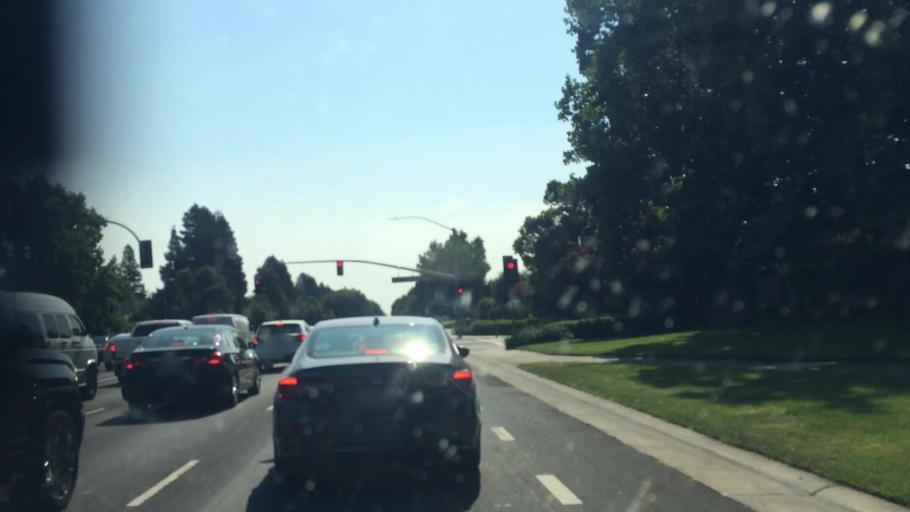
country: US
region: California
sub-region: Sacramento County
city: Laguna
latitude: 38.4233
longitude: -121.4384
